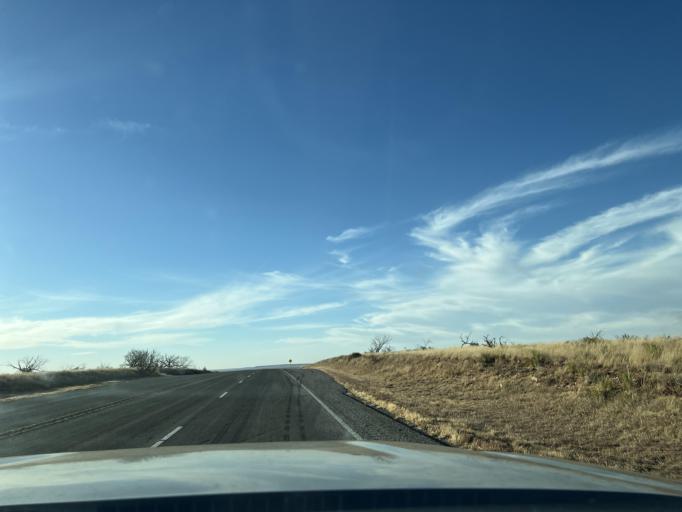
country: US
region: Texas
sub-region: Borden County
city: Gail
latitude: 32.7604
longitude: -101.2632
